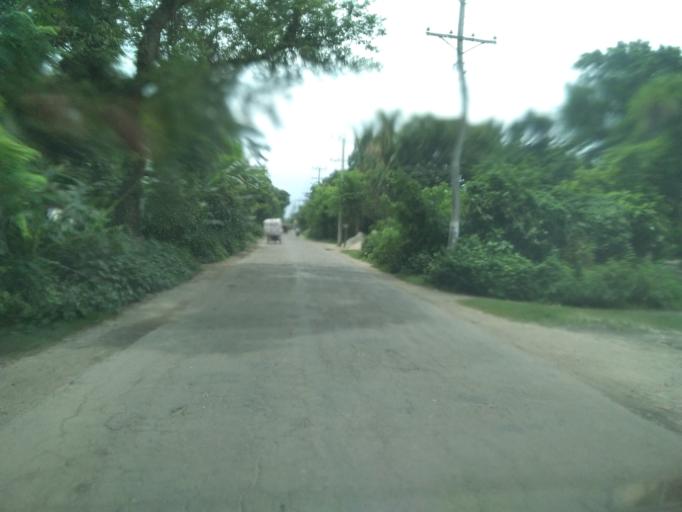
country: IN
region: West Bengal
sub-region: North 24 Parganas
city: Taki
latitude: 22.5739
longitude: 88.9998
